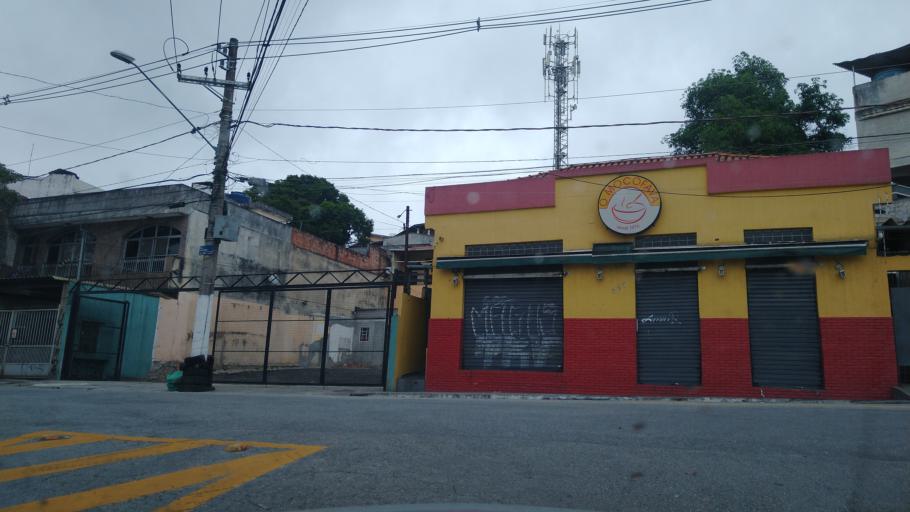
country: BR
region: Sao Paulo
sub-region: Sao Paulo
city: Sao Paulo
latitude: -23.4766
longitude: -46.6369
